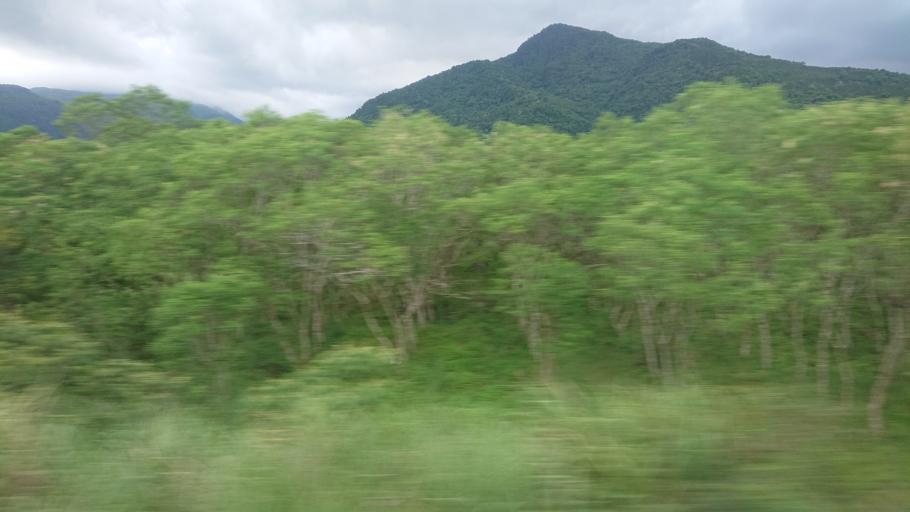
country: TW
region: Taiwan
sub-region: Hualien
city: Hualian
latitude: 23.6143
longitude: 121.3925
